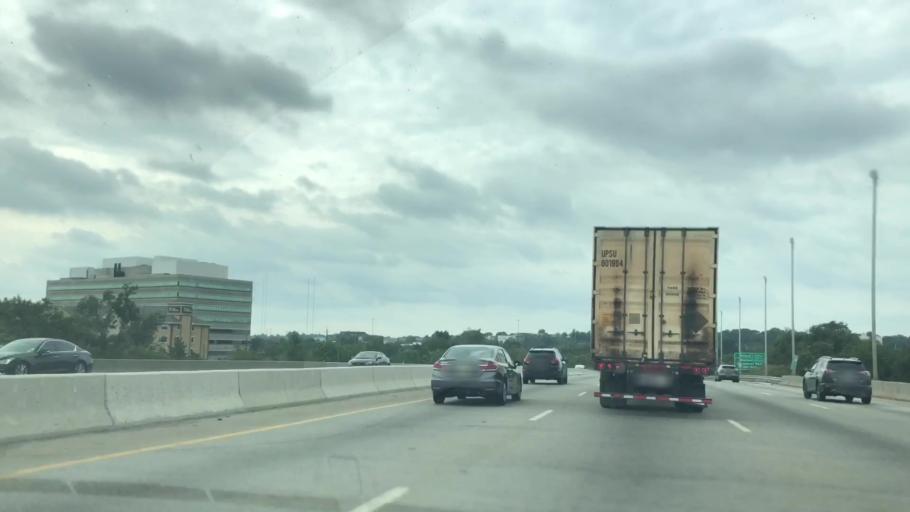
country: US
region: New Jersey
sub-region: Bergen County
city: Rutherford
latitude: 40.8108
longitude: -74.0932
